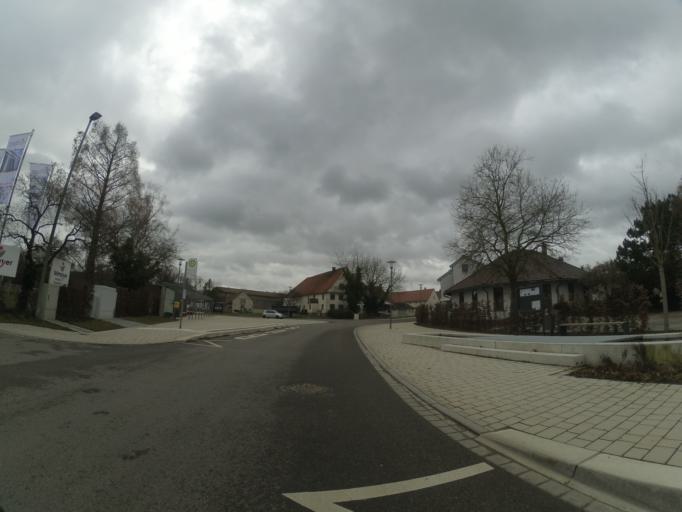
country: DE
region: Bavaria
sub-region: Swabia
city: Vohringen
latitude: 48.2885
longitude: 10.0997
